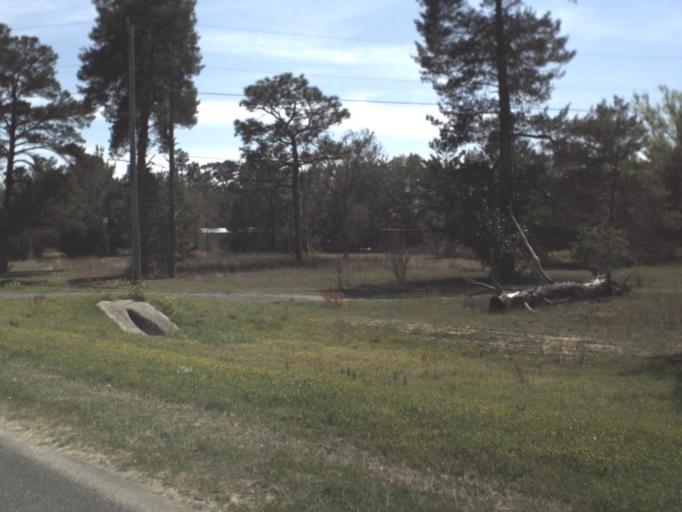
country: US
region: Florida
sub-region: Bay County
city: Lynn Haven
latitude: 30.3788
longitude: -85.6798
